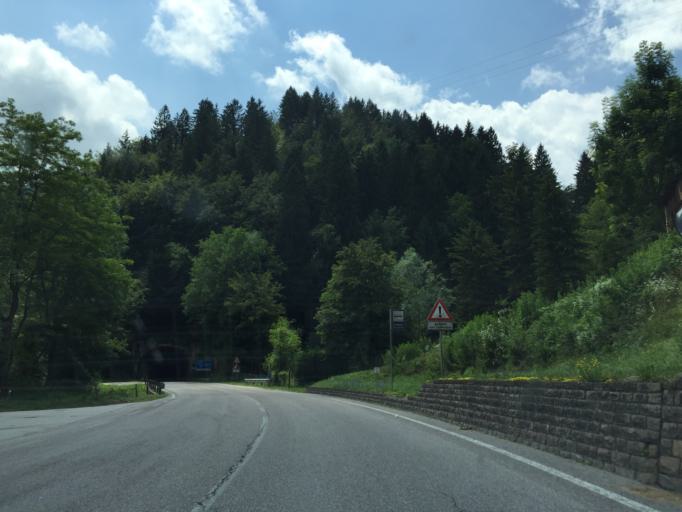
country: IT
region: Veneto
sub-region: Provincia di Belluno
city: Lamon
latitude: 46.0368
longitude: 11.7617
